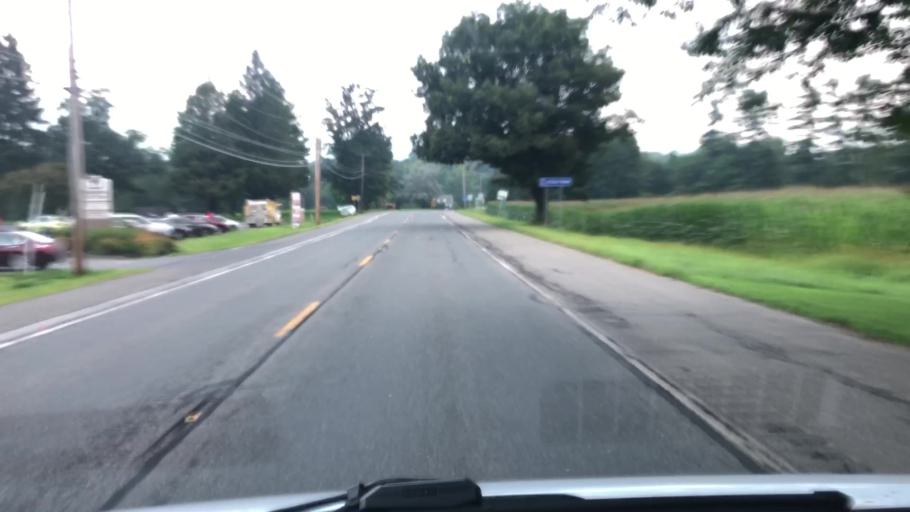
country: US
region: Massachusetts
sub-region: Berkshire County
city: Williamstown
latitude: 42.6568
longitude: -73.2397
